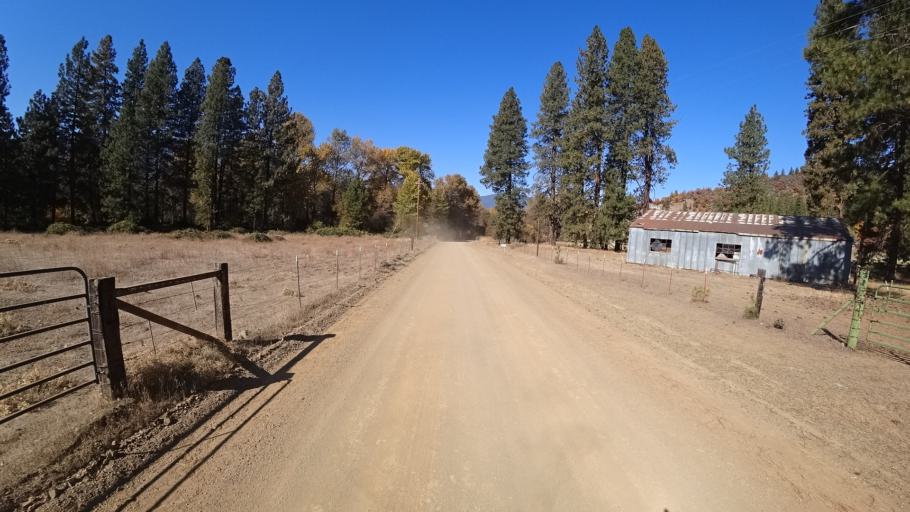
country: US
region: California
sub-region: Siskiyou County
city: Yreka
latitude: 41.6027
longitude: -122.9586
